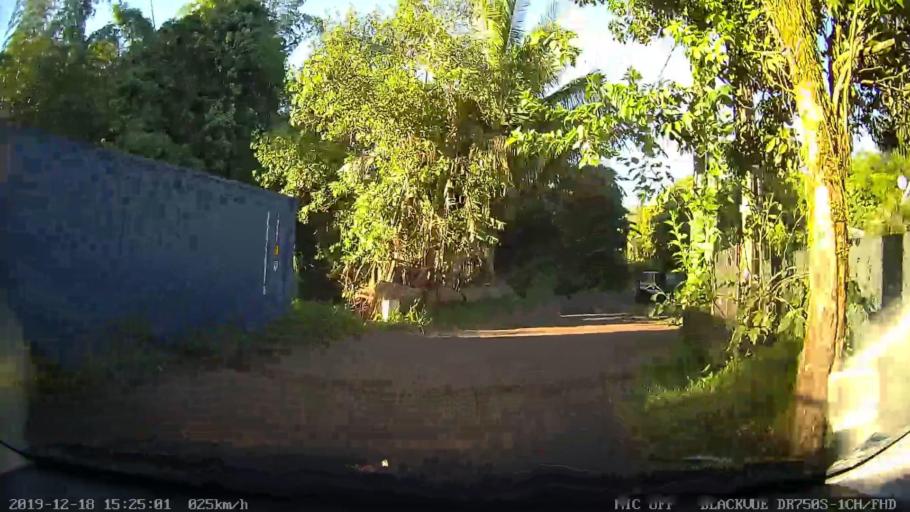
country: RE
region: Reunion
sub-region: Reunion
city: Bras-Panon
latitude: -21.0017
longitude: 55.6531
